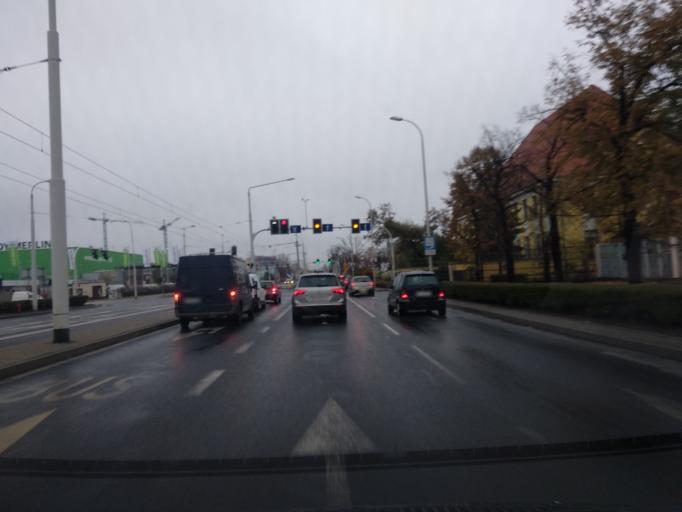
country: PL
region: Lower Silesian Voivodeship
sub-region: Powiat wroclawski
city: Wroclaw
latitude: 51.0894
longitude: 17.0659
